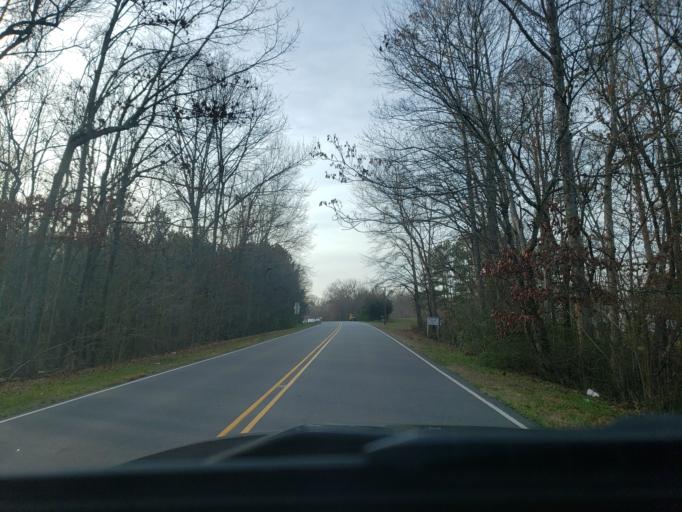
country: US
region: North Carolina
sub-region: Cleveland County
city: Boiling Springs
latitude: 35.3044
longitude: -81.7036
